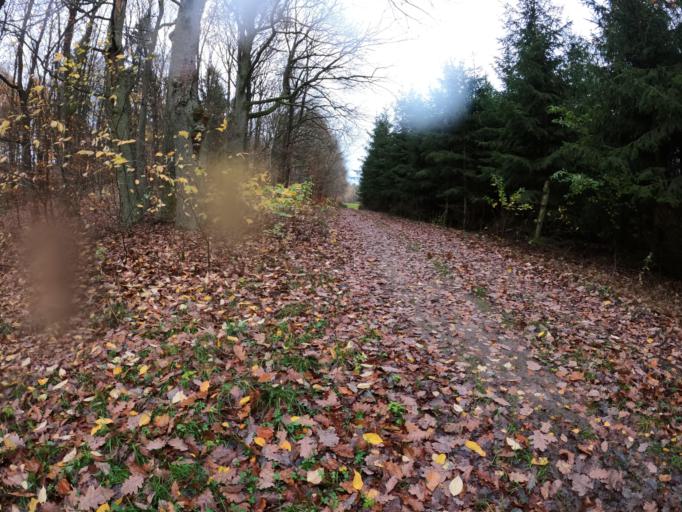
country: PL
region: West Pomeranian Voivodeship
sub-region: Powiat walecki
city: Tuczno
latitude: 53.2516
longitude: 16.2275
